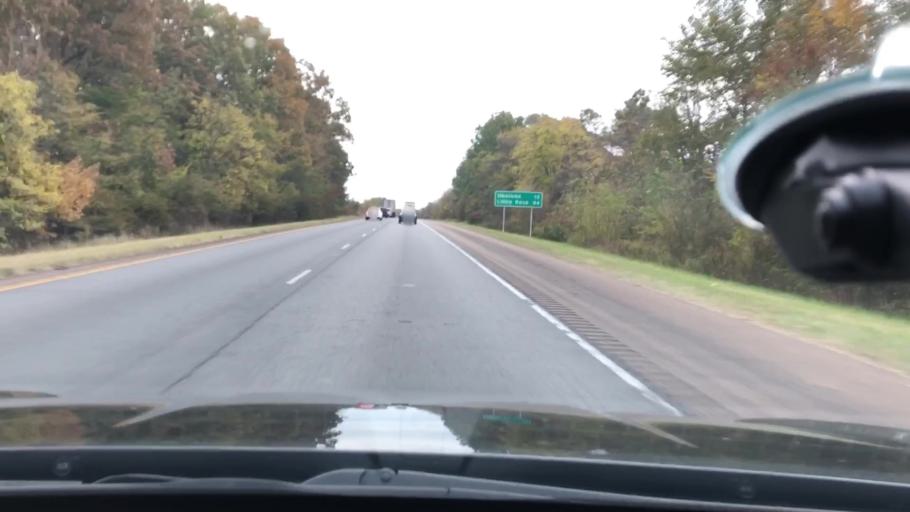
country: US
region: Arkansas
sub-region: Nevada County
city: Prescott
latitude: 33.8395
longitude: -93.3842
